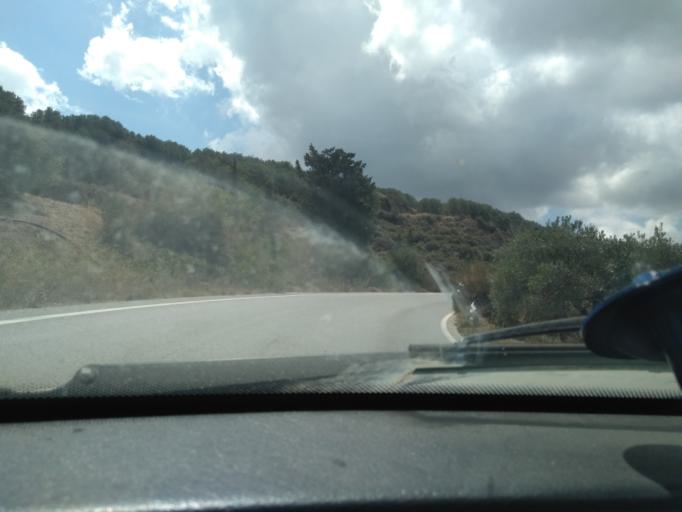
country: GR
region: Crete
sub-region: Nomos Lasithiou
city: Siteia
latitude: 35.0988
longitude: 26.0721
